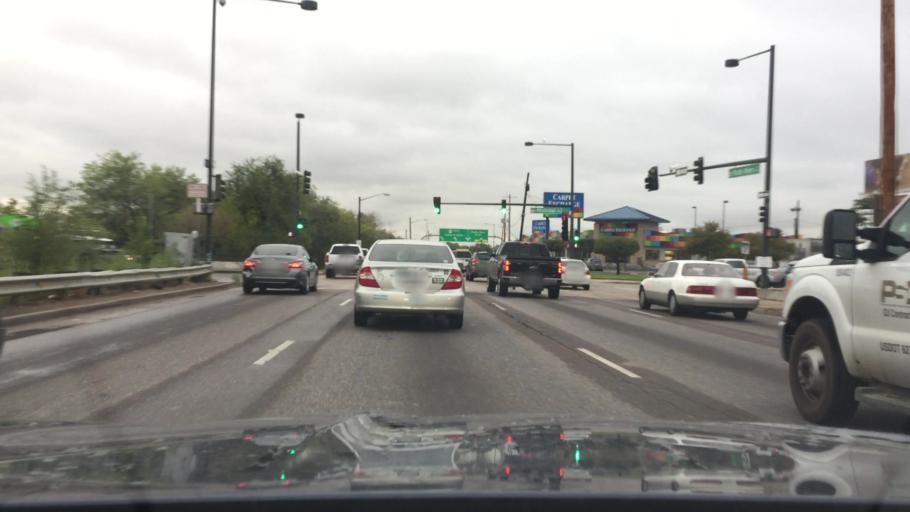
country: US
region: Colorado
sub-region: Denver County
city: Denver
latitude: 39.6971
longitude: -104.9928
